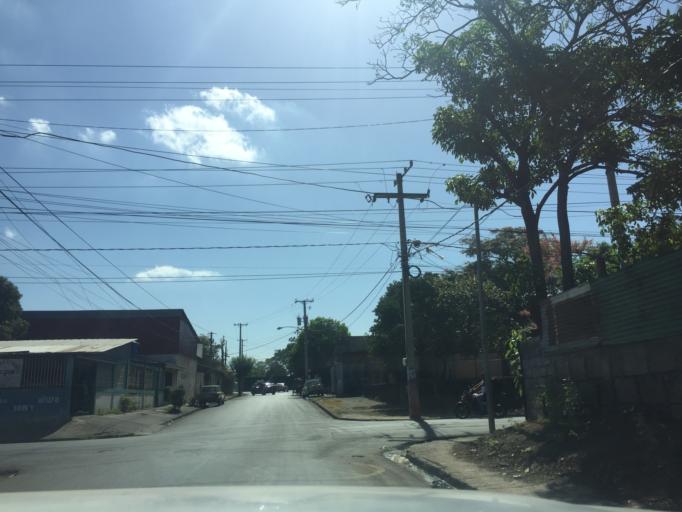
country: NI
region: Managua
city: Managua
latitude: 12.1501
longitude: -86.2543
